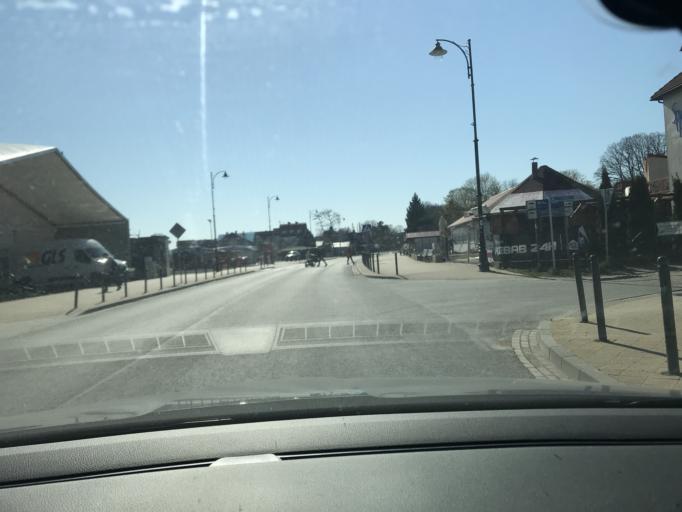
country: PL
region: Pomeranian Voivodeship
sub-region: Powiat nowodworski
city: Krynica Morska
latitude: 54.3794
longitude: 19.4424
